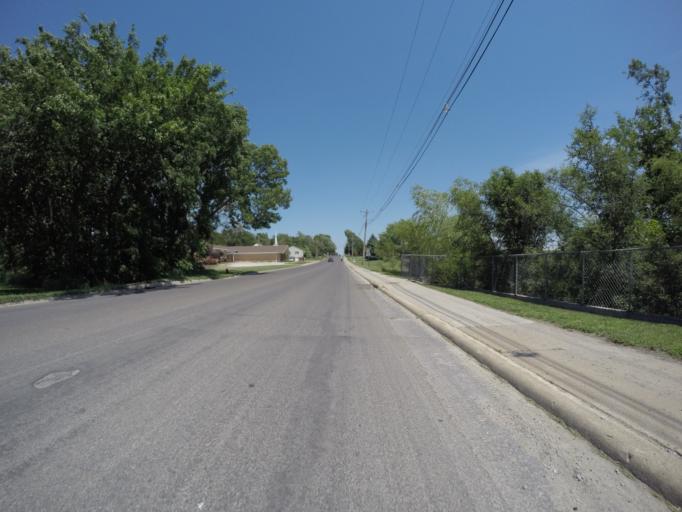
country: US
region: Kansas
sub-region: Nemaha County
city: Sabetha
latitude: 39.8997
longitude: -95.7957
